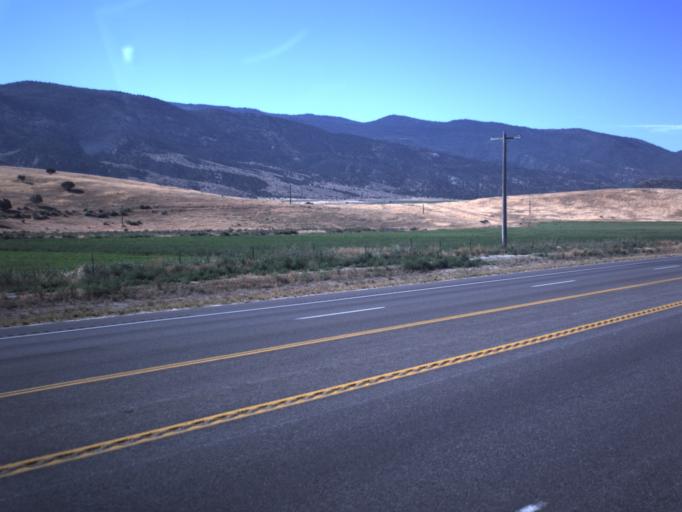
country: US
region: Utah
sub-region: Sanpete County
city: Manti
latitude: 39.3046
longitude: -111.6159
